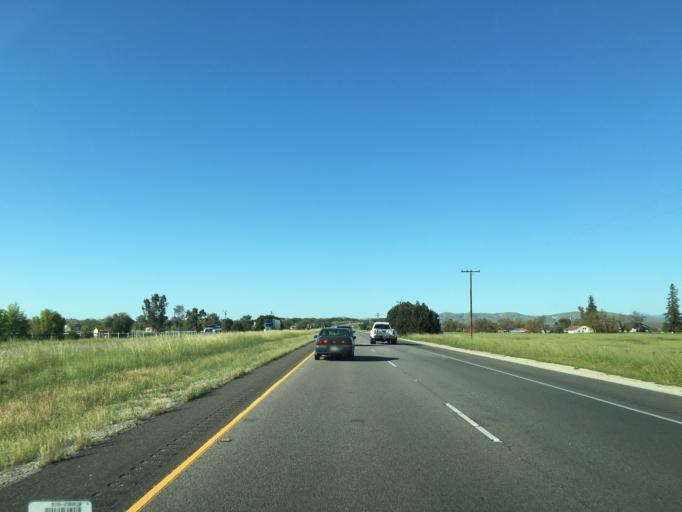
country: US
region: California
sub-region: San Luis Obispo County
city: Paso Robles
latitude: 35.6886
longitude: -120.6966
